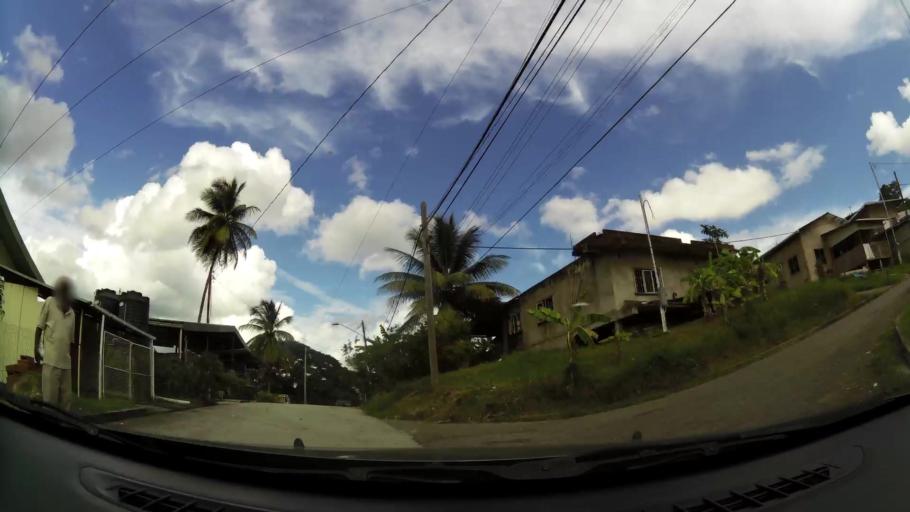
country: TT
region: City of San Fernando
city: Mon Repos
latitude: 10.2761
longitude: -61.4477
